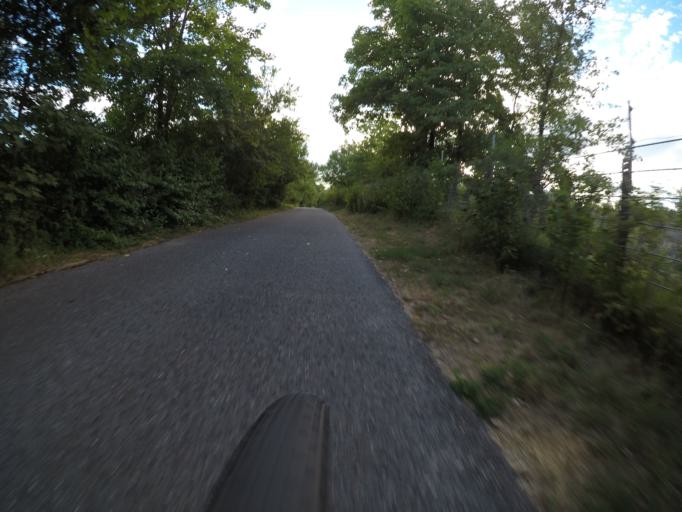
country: DE
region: Baden-Wuerttemberg
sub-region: Regierungsbezirk Stuttgart
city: Ehningen
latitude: 48.6952
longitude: 8.9466
